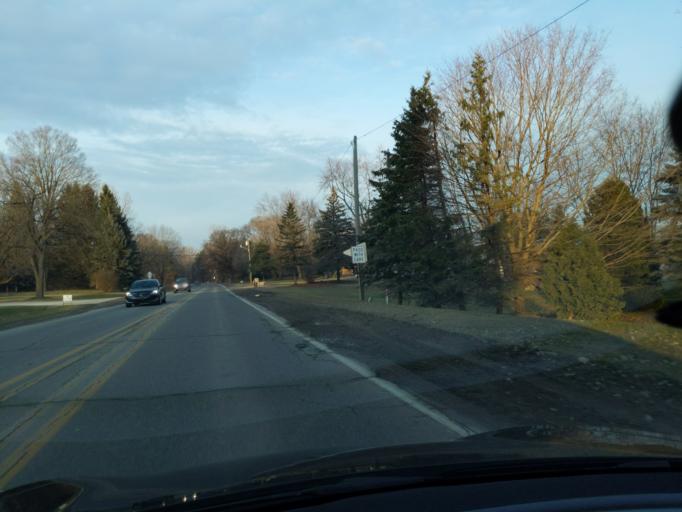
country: US
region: Michigan
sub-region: Livingston County
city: Brighton
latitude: 42.6011
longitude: -83.7504
